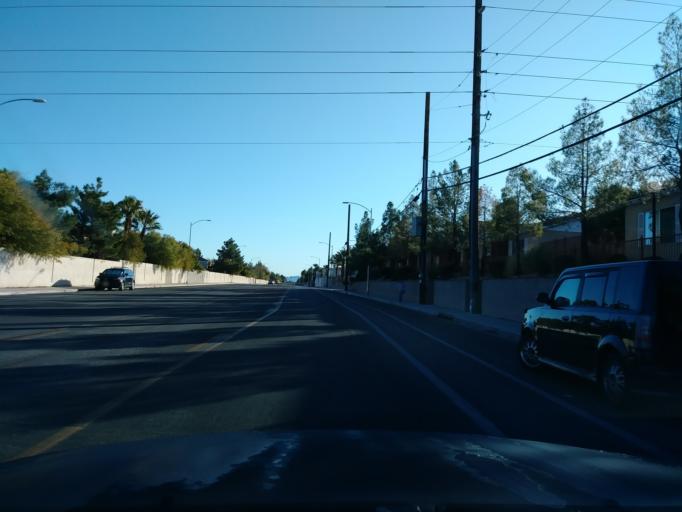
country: US
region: Nevada
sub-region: Clark County
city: Spring Valley
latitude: 36.1573
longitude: -115.2712
